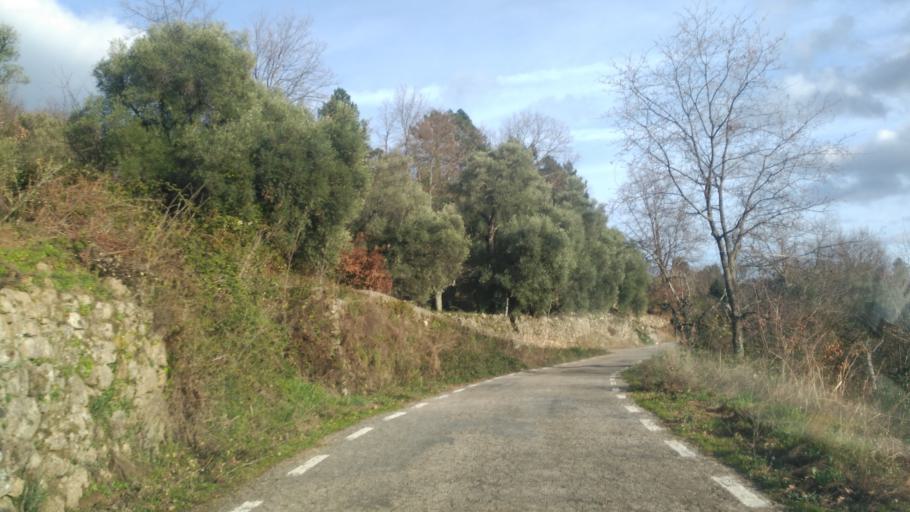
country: ES
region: Castille and Leon
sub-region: Provincia de Salamanca
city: Sequeros
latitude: 40.5037
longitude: -6.0388
